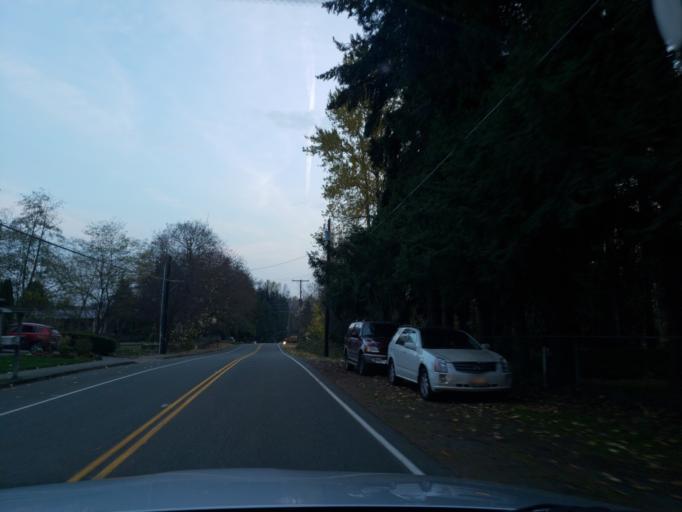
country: US
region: Washington
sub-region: King County
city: Kenmore
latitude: 47.7718
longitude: -122.2404
